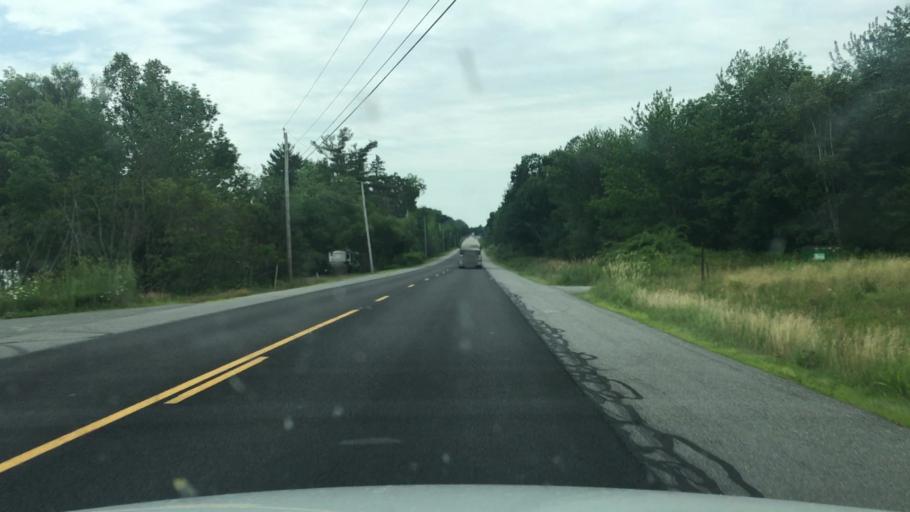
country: US
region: Maine
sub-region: Knox County
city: Washington
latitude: 44.3942
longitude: -69.3518
